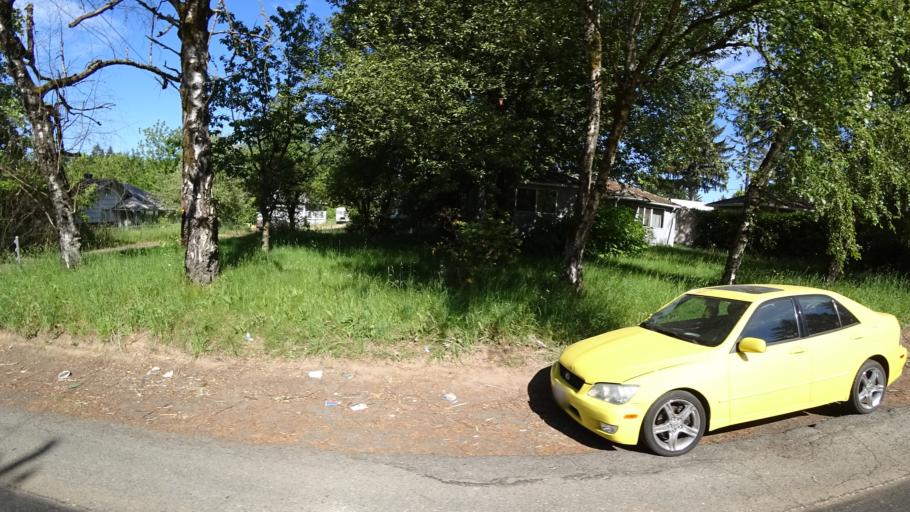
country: US
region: Oregon
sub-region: Washington County
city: Metzger
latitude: 45.4396
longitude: -122.7654
